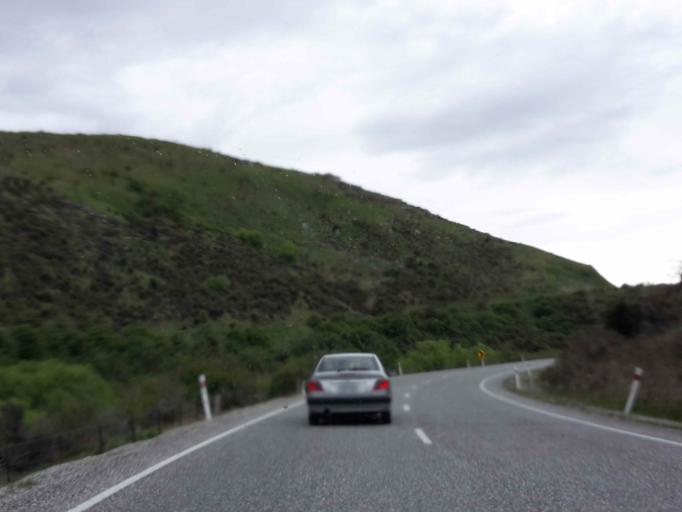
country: NZ
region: Otago
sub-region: Queenstown-Lakes District
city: Wanaka
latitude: -44.7367
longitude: 169.5069
